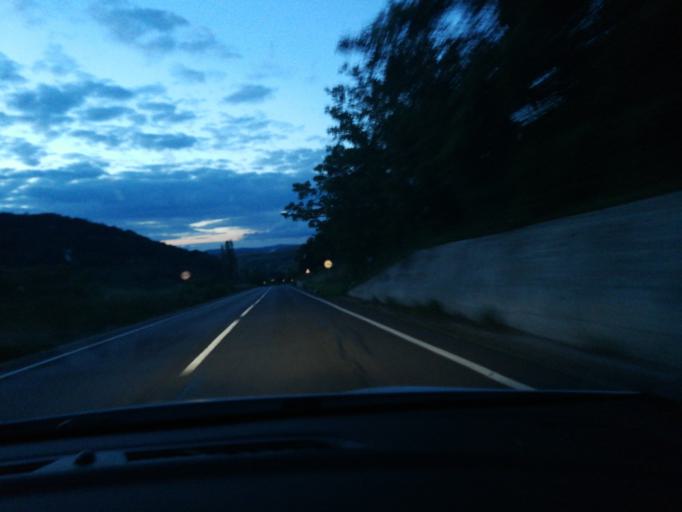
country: RO
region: Mures
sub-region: Comuna Saschiz
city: Saschiz
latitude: 46.2187
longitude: 24.9725
